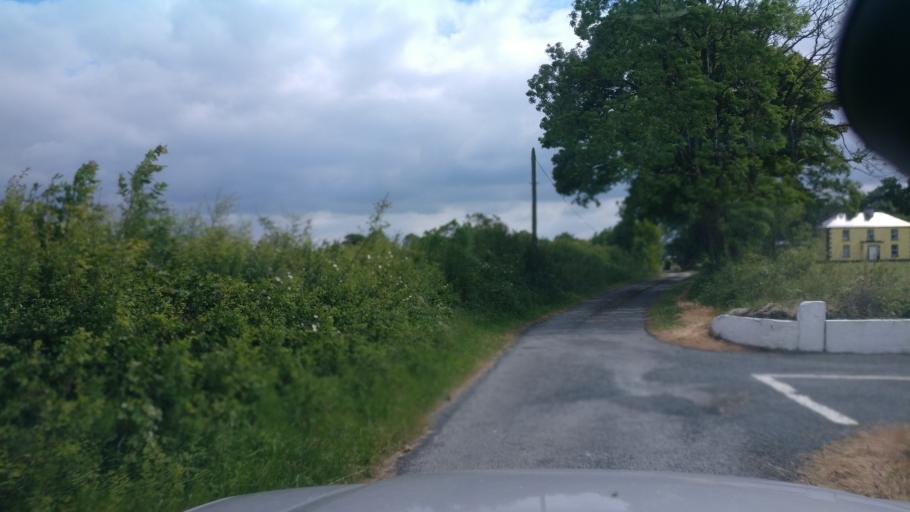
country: IE
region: Connaught
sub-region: County Galway
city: Ballinasloe
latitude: 53.2737
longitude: -8.3346
